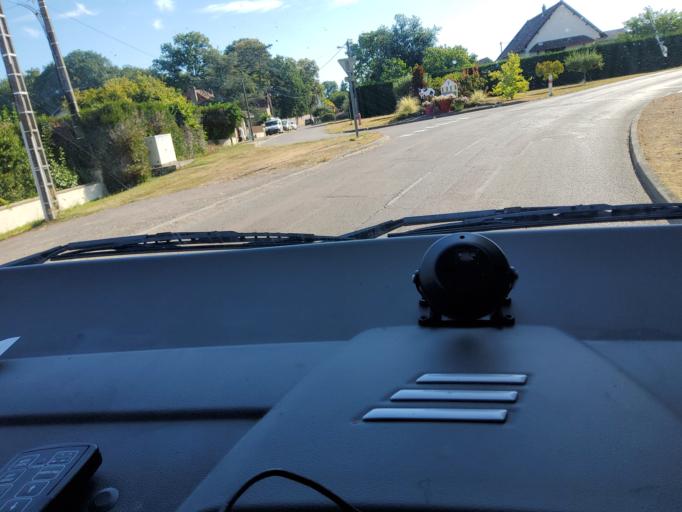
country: FR
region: Bourgogne
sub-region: Departement de la Cote-d'Or
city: Brazey-en-Plaine
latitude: 47.1408
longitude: 5.2421
